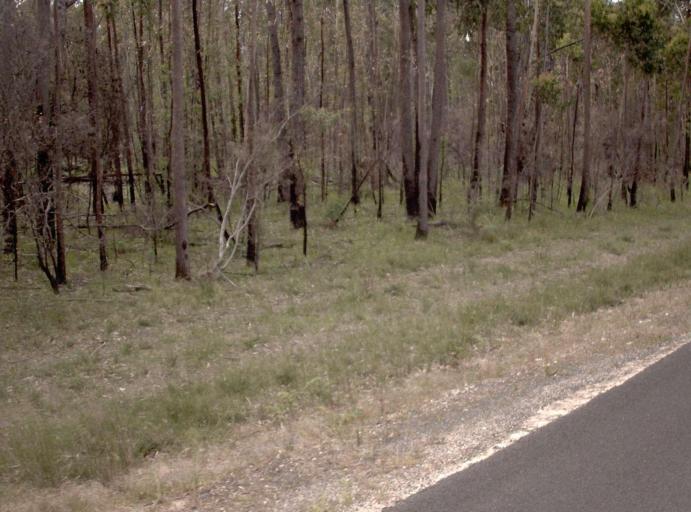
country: AU
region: New South Wales
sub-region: Bega Valley
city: Eden
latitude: -37.5100
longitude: 149.5152
